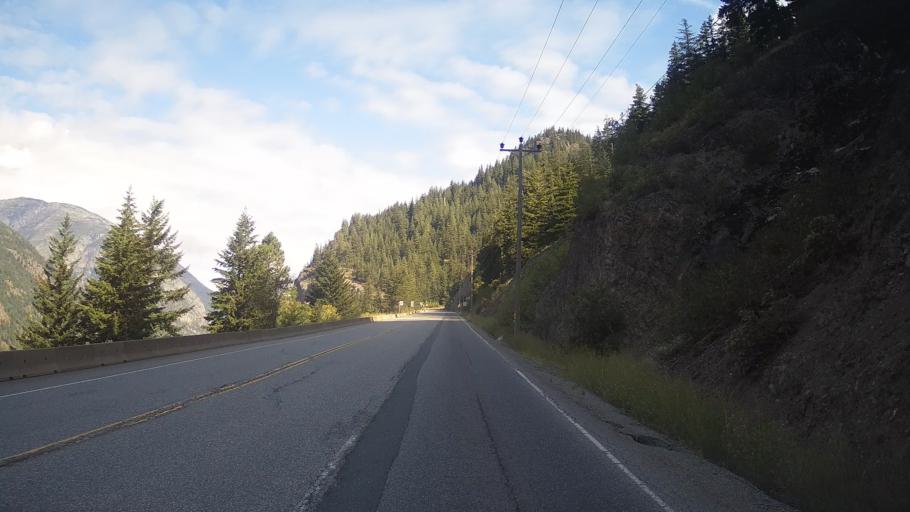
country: CA
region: British Columbia
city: Hope
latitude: 50.0700
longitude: -121.5458
